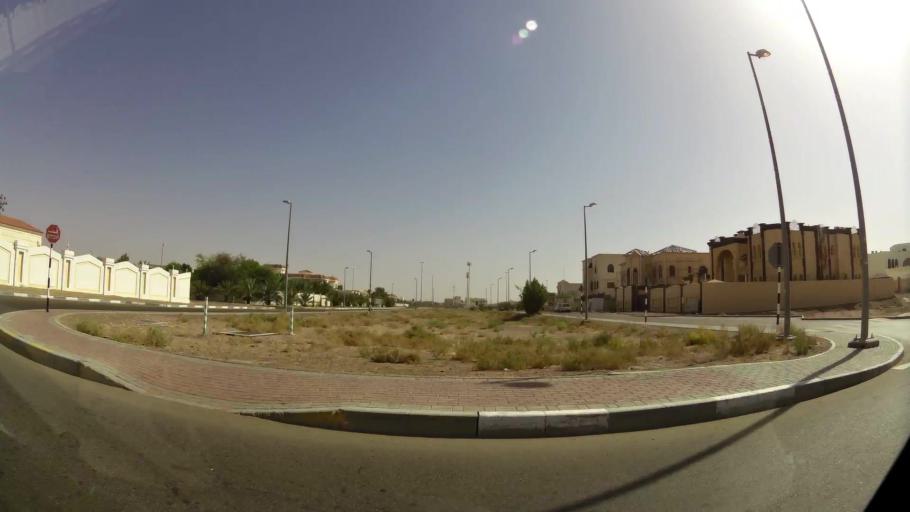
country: OM
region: Al Buraimi
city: Al Buraymi
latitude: 24.3386
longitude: 55.8003
